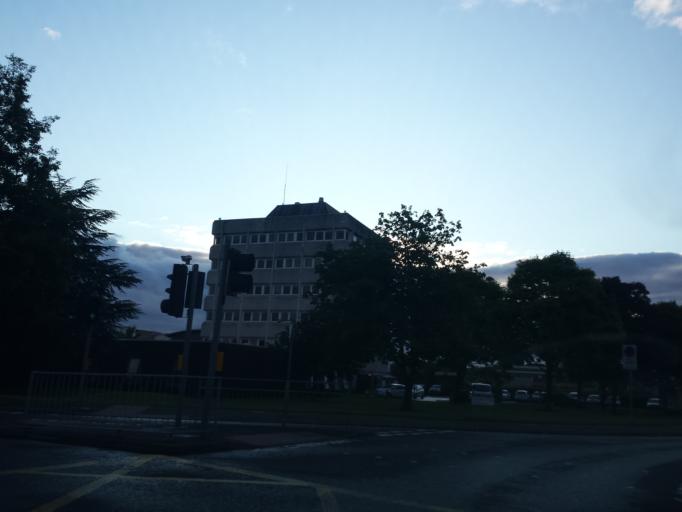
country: GB
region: Scotland
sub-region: Perth and Kinross
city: Perth
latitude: 56.3992
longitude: -3.4366
